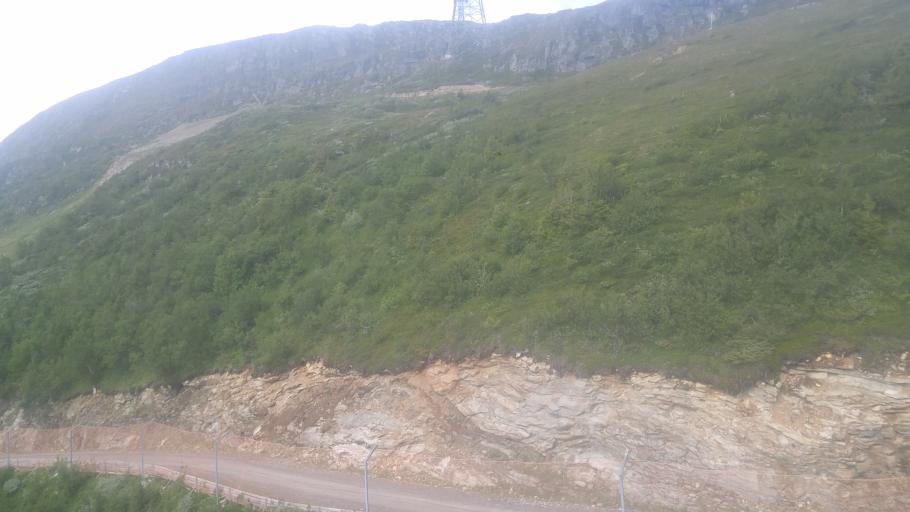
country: SE
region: Jaemtland
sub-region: Are Kommun
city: Are
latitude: 63.4113
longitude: 13.0773
